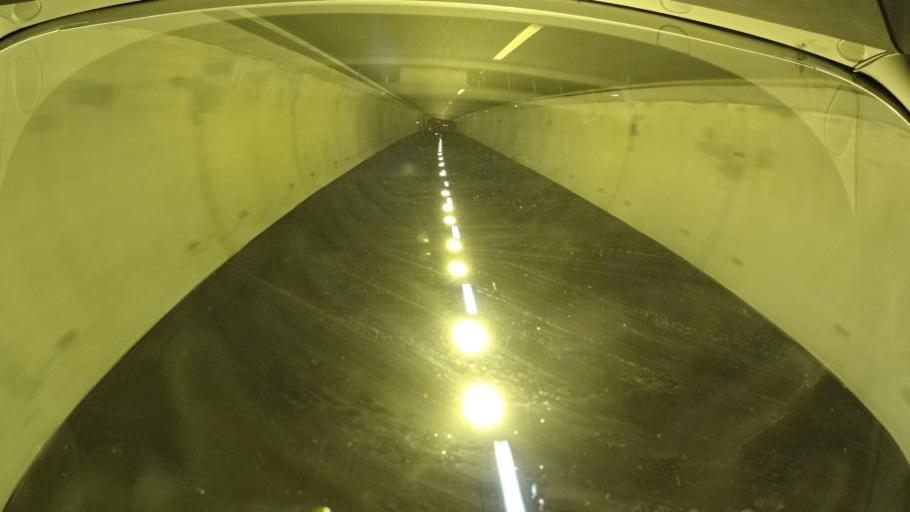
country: NO
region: Sor-Trondelag
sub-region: Trondheim
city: Trondheim
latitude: 63.4277
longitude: 10.5096
